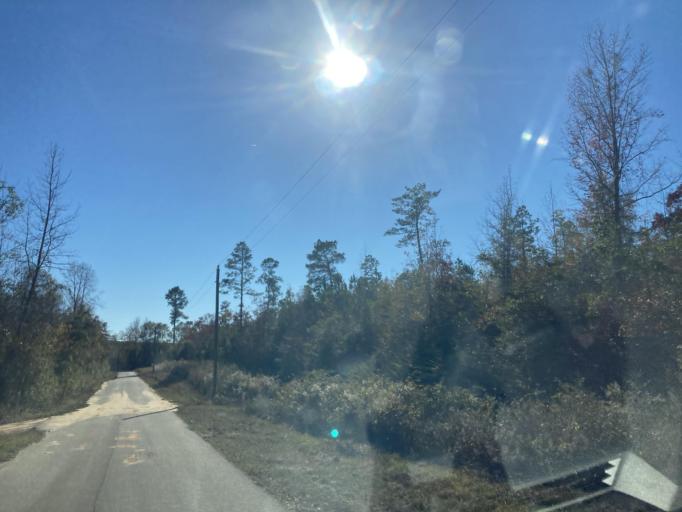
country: US
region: Mississippi
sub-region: Lamar County
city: Sumrall
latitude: 31.3342
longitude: -89.6221
